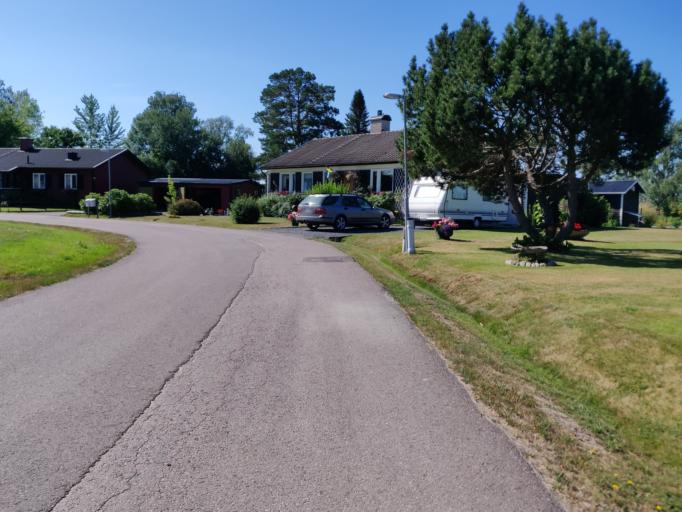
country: SE
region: Vaermland
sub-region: Hagfors Kommun
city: Hagfors
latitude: 59.9992
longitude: 13.5883
